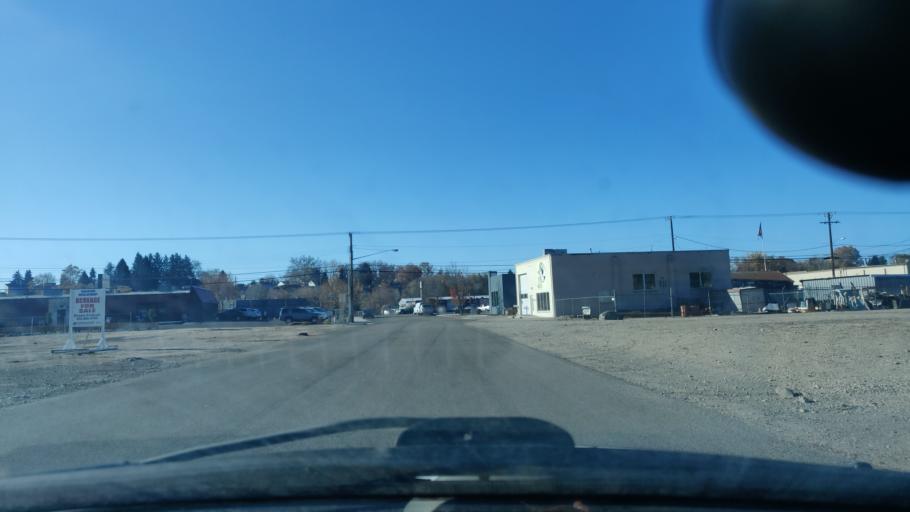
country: US
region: Idaho
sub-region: Ada County
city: Garden City
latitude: 43.6235
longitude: -116.2379
